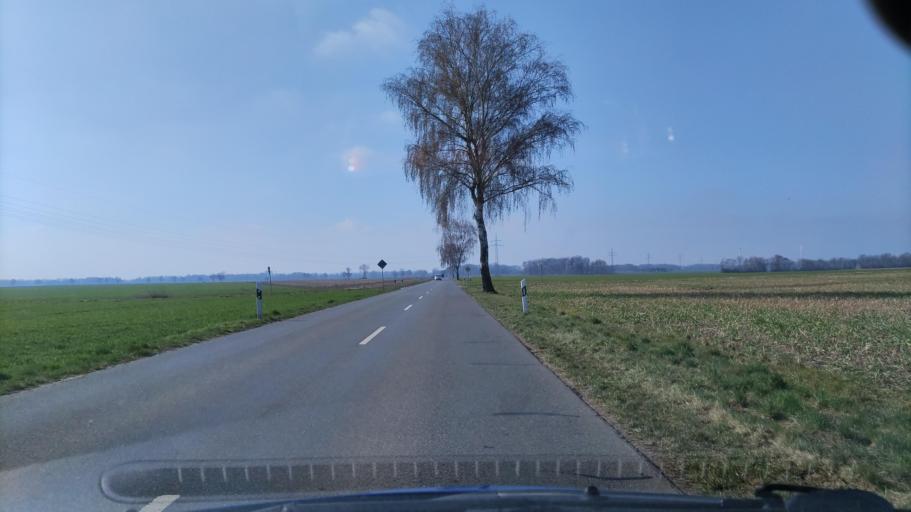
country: DE
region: Lower Saxony
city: Kusten
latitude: 52.9545
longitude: 11.0621
